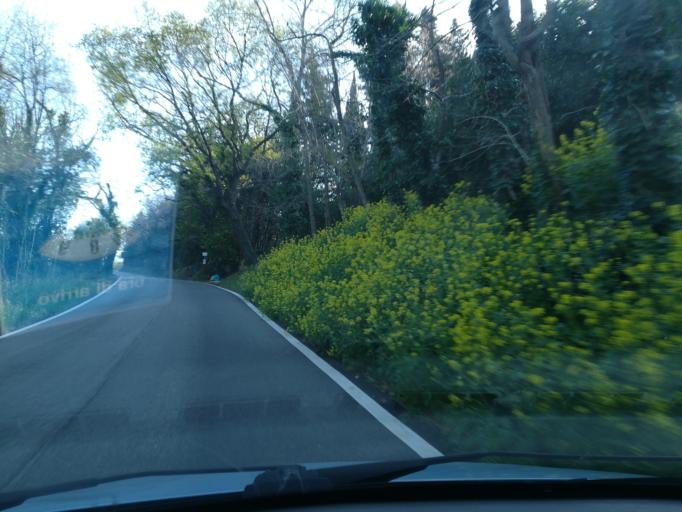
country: IT
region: The Marches
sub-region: Provincia di Macerata
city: Villa Potenza
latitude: 43.3190
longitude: 13.4362
